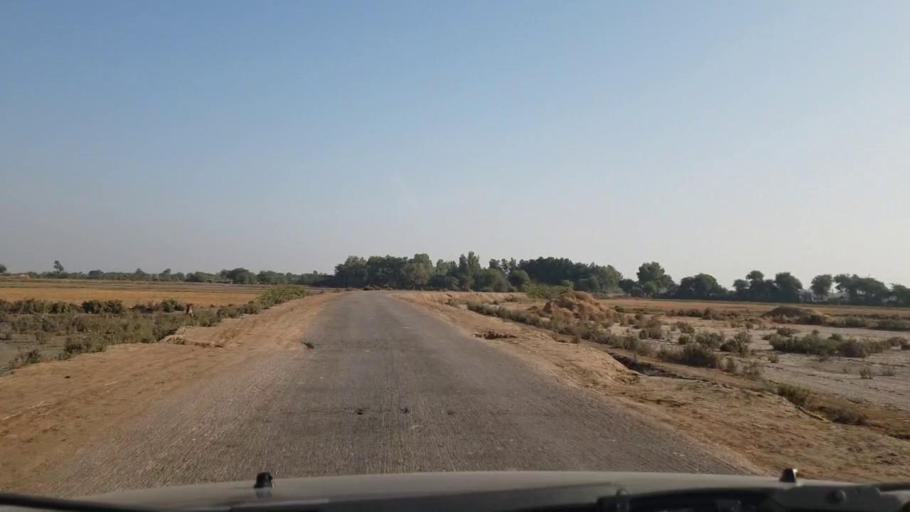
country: PK
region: Sindh
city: Tando Bago
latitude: 24.8726
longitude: 69.0582
